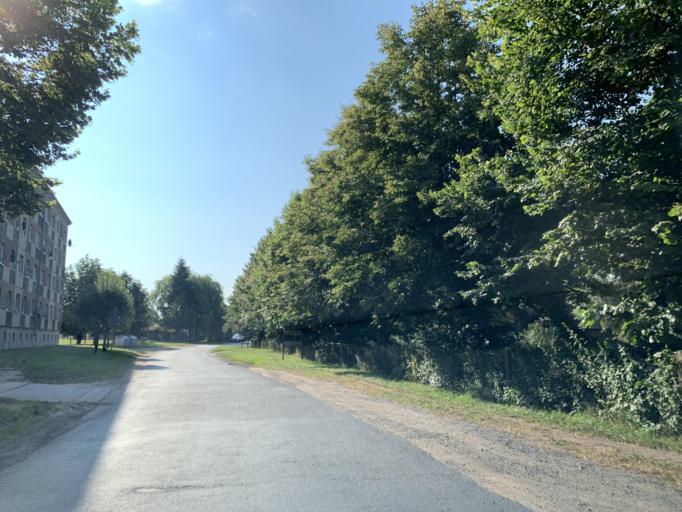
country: DE
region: Mecklenburg-Vorpommern
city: Loitz
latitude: 53.3553
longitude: 13.3534
